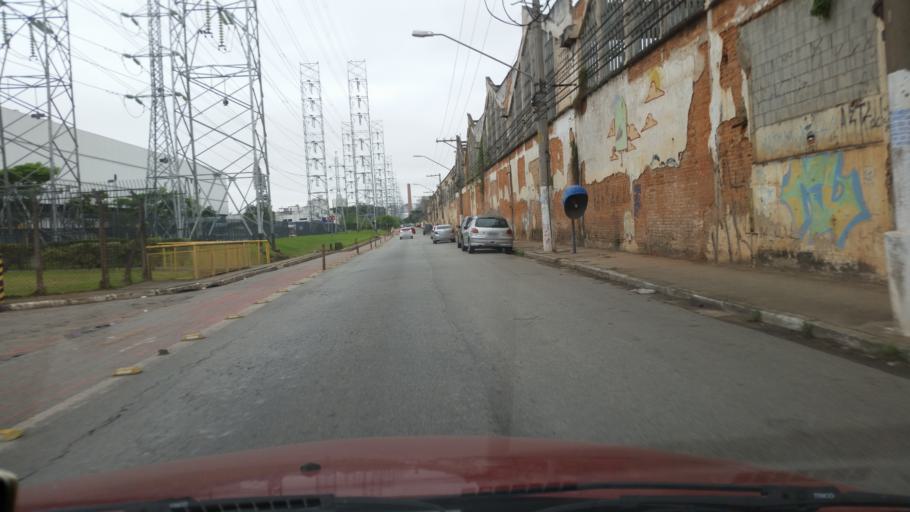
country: BR
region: Sao Paulo
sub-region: Sao Caetano Do Sul
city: Sao Caetano do Sul
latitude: -23.5948
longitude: -46.5861
